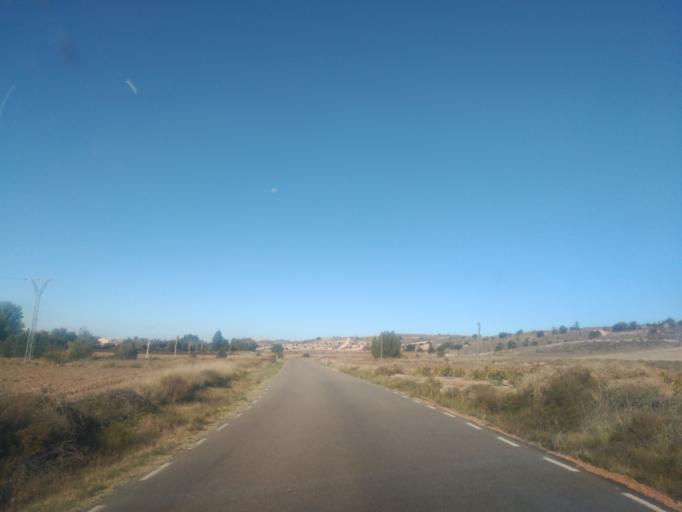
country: ES
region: Castille and Leon
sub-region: Provincia de Burgos
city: Penaranda de Duero
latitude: 41.6861
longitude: -3.4379
